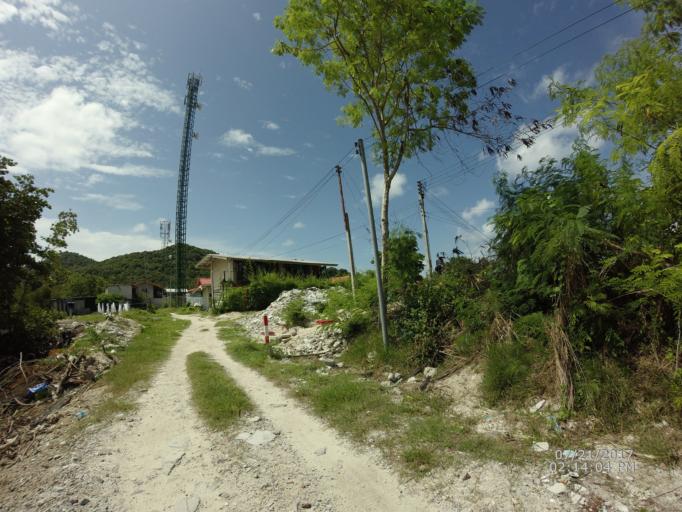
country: TH
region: Phangnga
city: Ban Phru Nai
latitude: 7.7606
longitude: 98.7696
